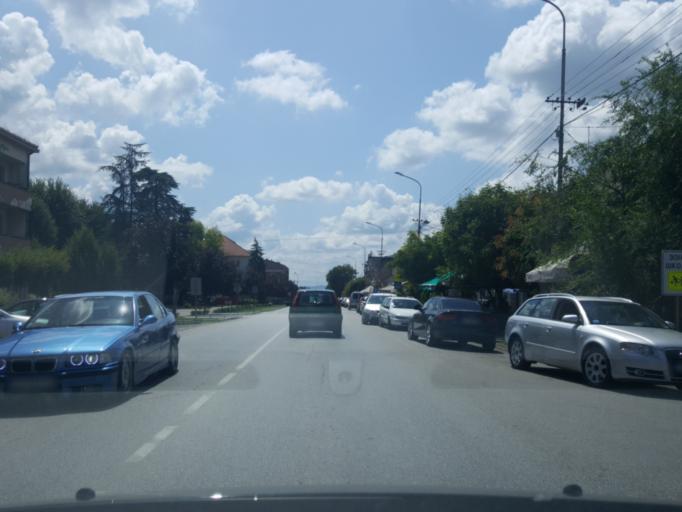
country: RS
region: Central Serbia
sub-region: Macvanski Okrug
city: Bogatic
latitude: 44.8365
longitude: 19.4802
